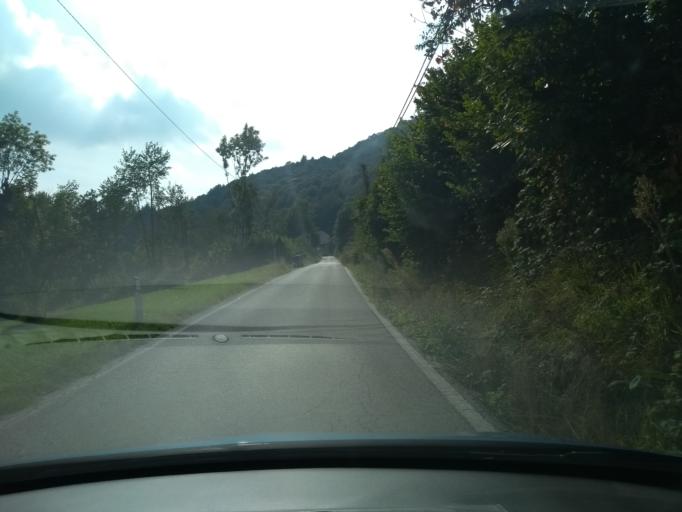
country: IT
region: Piedmont
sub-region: Provincia di Torino
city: Corio
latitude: 45.3152
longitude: 7.5220
